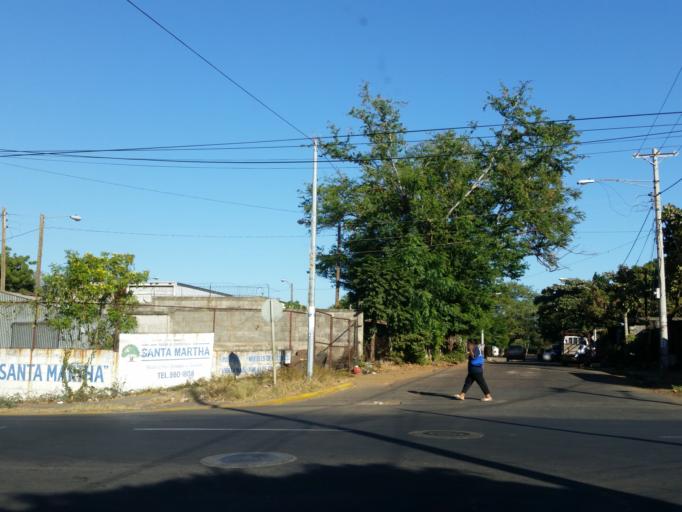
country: NI
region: Managua
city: Managua
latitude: 12.1230
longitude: -86.2960
